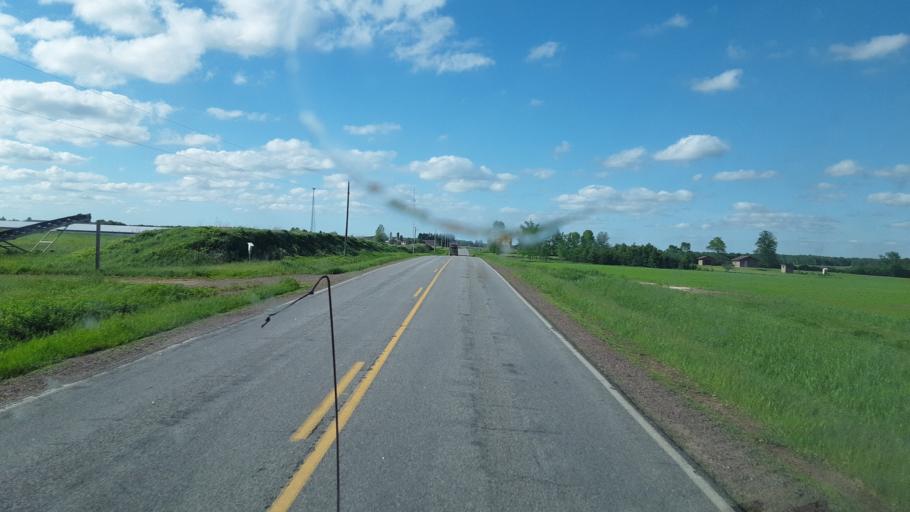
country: US
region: Wisconsin
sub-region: Wood County
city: Marshfield
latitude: 44.4283
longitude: -90.1597
